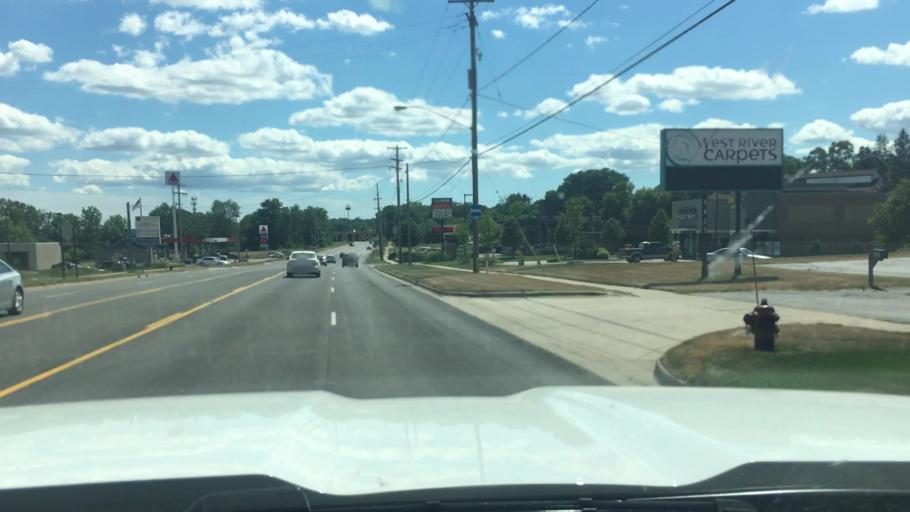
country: US
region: Michigan
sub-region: Kent County
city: Comstock Park
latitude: 43.0471
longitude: -85.6563
